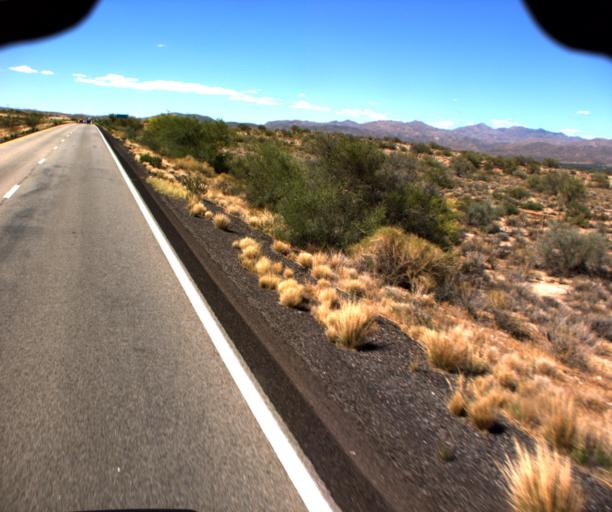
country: US
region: Arizona
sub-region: Mohave County
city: Kingman
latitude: 34.8724
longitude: -113.6451
